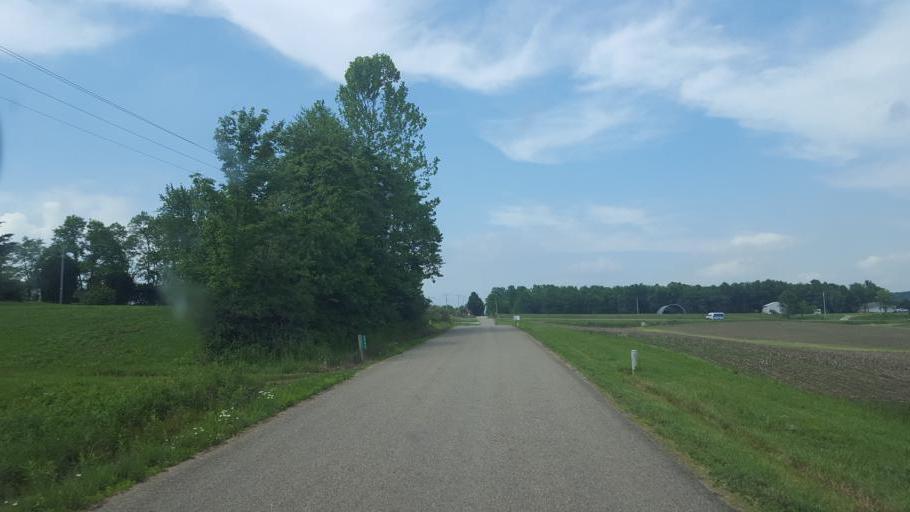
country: US
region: Ohio
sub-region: Knox County
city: Oak Hill
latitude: 40.2843
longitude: -82.2425
